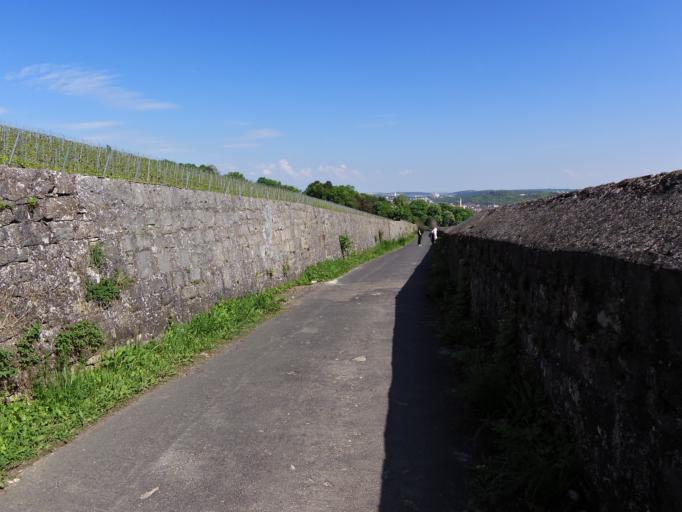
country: DE
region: Bavaria
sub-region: Regierungsbezirk Unterfranken
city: Wuerzburg
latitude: 49.8069
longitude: 9.9350
